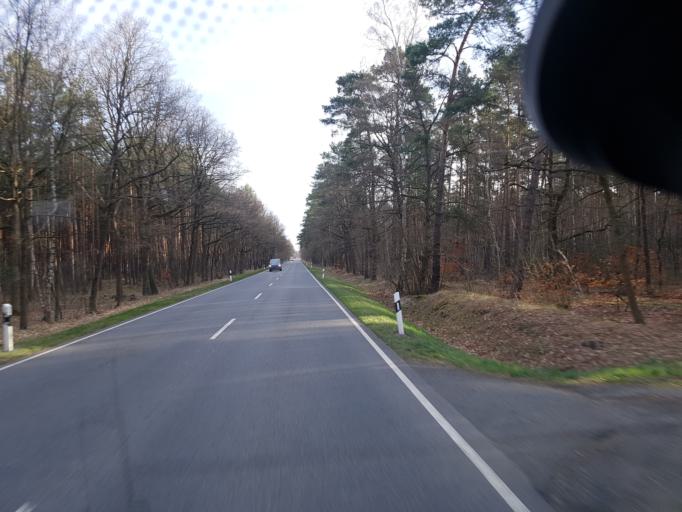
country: DE
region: Brandenburg
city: Luebben
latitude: 51.9664
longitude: 13.9477
